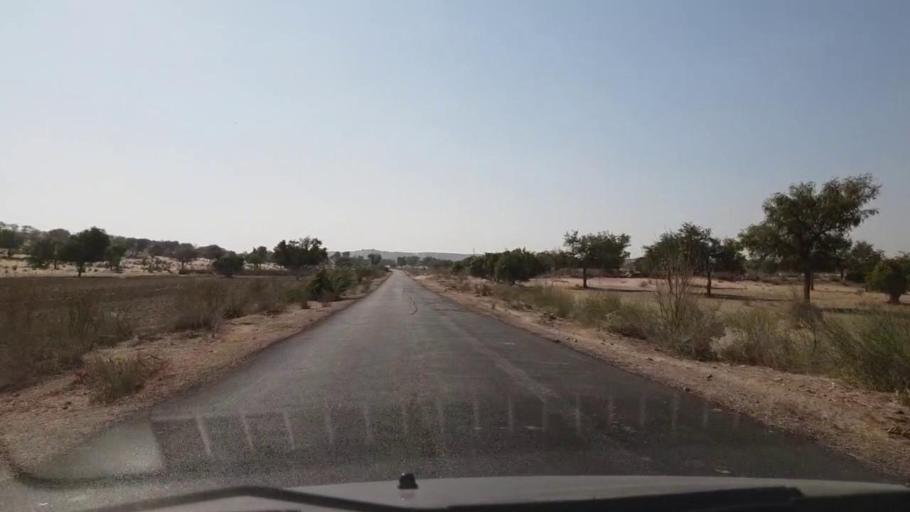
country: PK
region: Sindh
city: Mithi
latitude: 24.6635
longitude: 69.7597
